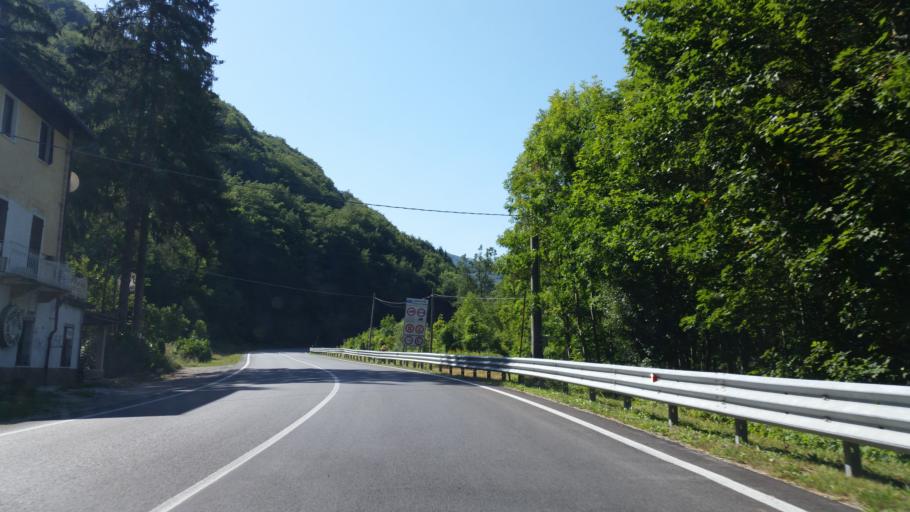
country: IT
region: Piedmont
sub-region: Provincia di Cuneo
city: Limone Piemonte
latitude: 44.2142
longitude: 7.5718
